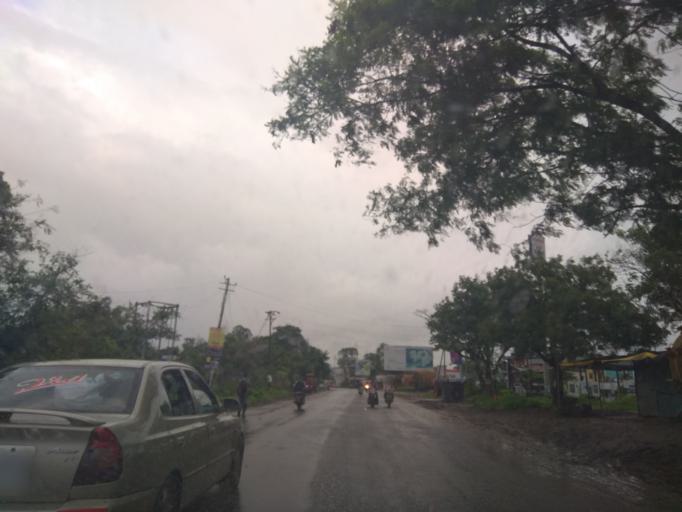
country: IN
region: Maharashtra
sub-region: Pune Division
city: Kharakvasla
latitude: 18.5114
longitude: 73.6829
